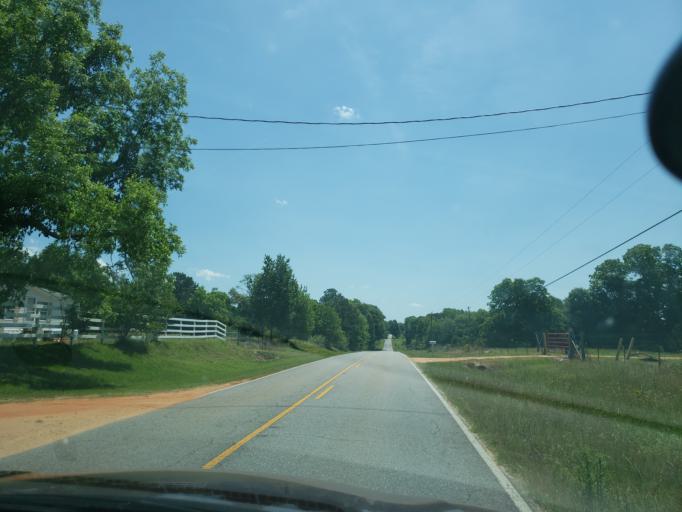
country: US
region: Alabama
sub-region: Elmore County
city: Tallassee
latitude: 32.5809
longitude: -85.8043
